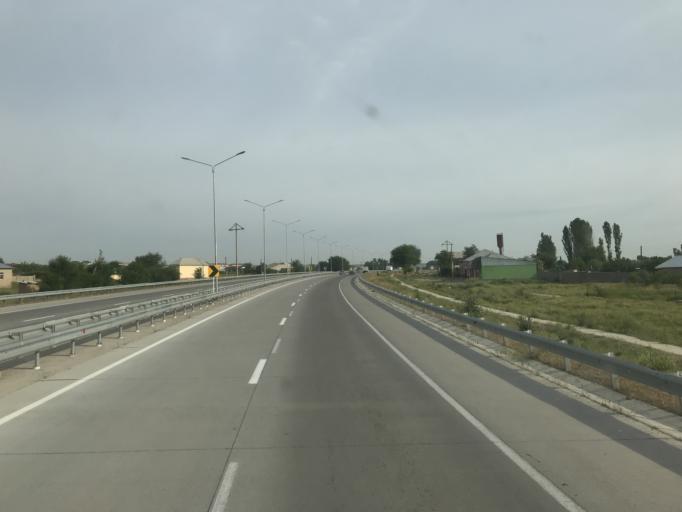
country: KZ
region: Ongtustik Qazaqstan
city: Qazyqurt
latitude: 41.7874
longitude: 69.3941
